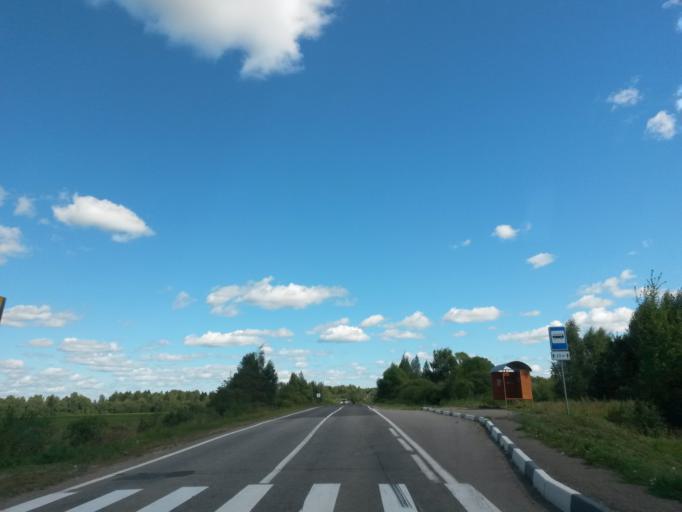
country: RU
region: Jaroslavl
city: Yaroslavl
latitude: 57.8008
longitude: 39.8103
